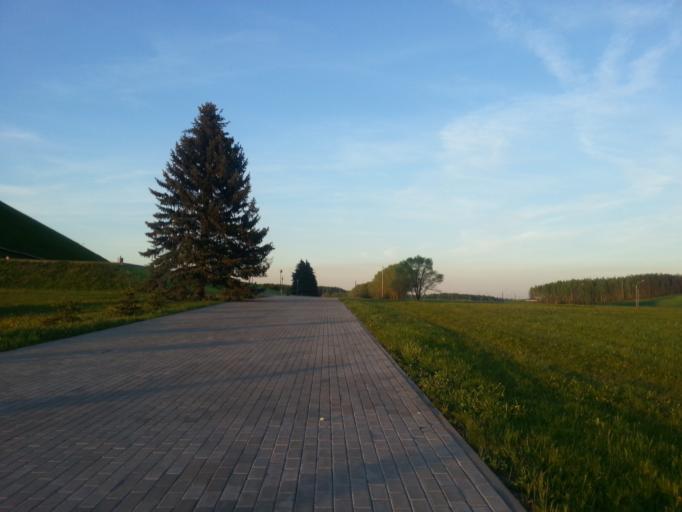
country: BY
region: Minsk
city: Slabada
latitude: 54.0178
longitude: 27.8970
